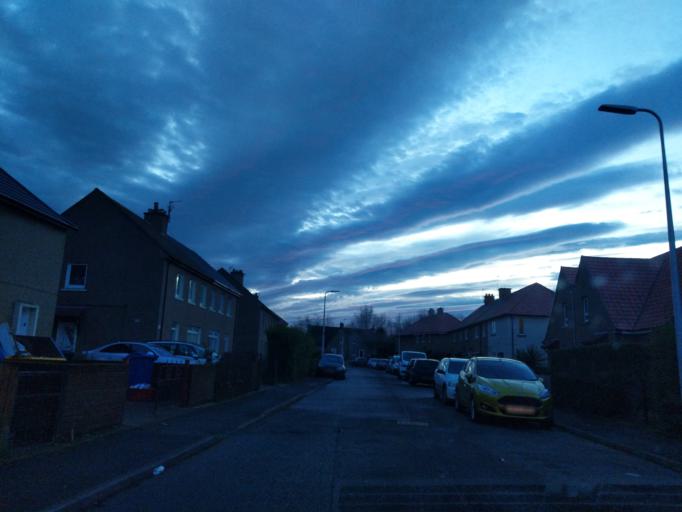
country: GB
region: Scotland
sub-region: Midlothian
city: Loanhead
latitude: 55.8683
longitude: -3.1825
